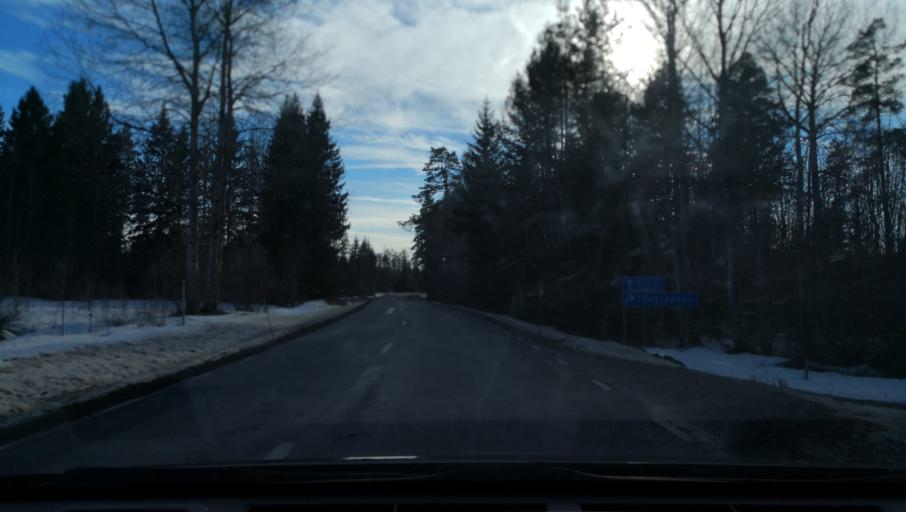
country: SE
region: Uppsala
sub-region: Osthammars Kommun
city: Osterbybruk
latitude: 60.2623
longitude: 17.9522
